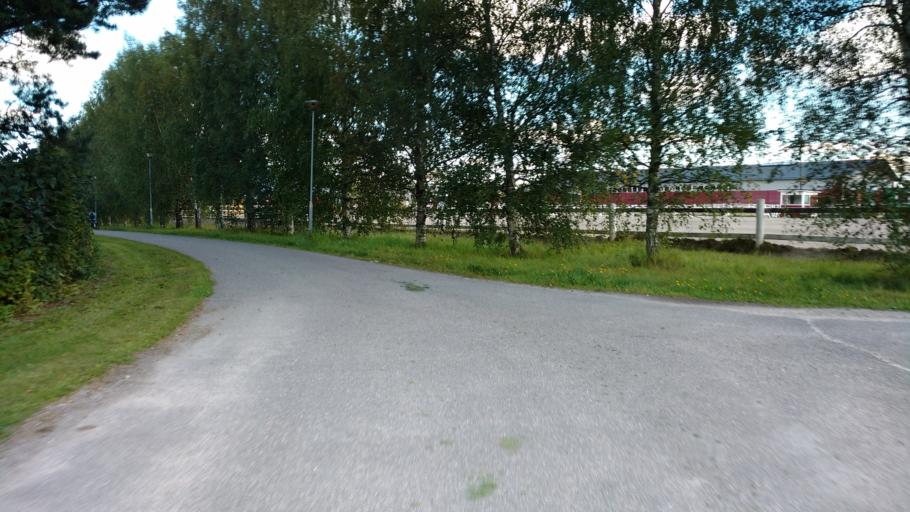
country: FI
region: Varsinais-Suomi
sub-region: Salo
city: Salo
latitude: 60.3797
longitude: 23.1429
